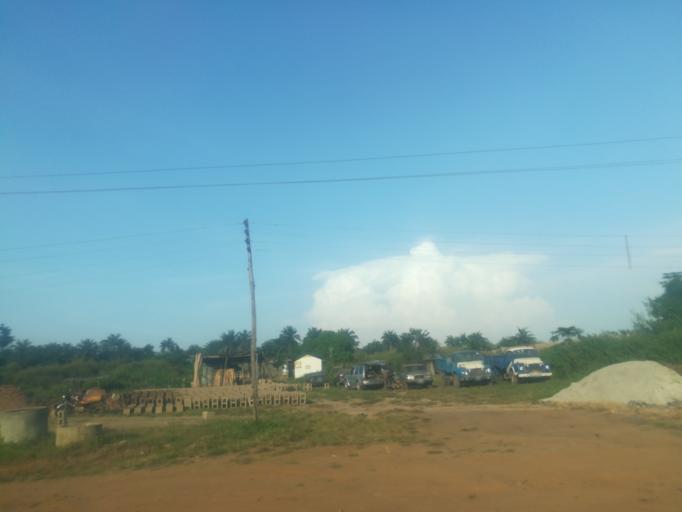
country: NG
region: Oyo
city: Moniya
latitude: 7.5487
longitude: 3.8930
